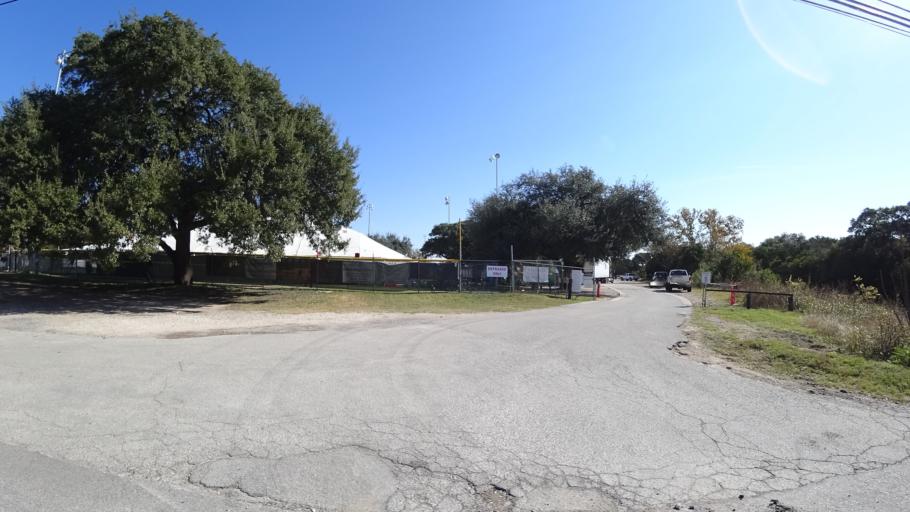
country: US
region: Texas
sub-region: Travis County
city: Barton Creek
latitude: 30.2342
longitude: -97.8577
